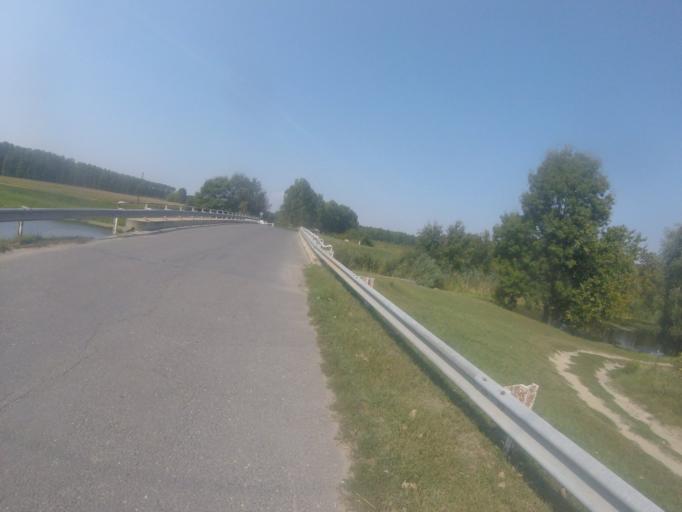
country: HU
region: Bacs-Kiskun
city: Ersekcsanad
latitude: 46.2526
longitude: 18.9719
